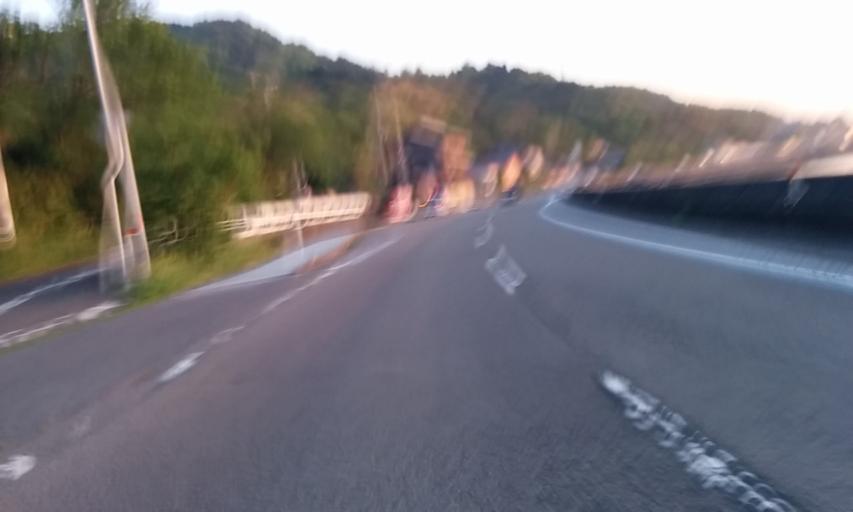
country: JP
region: Ehime
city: Iyo
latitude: 33.6808
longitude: 132.6285
